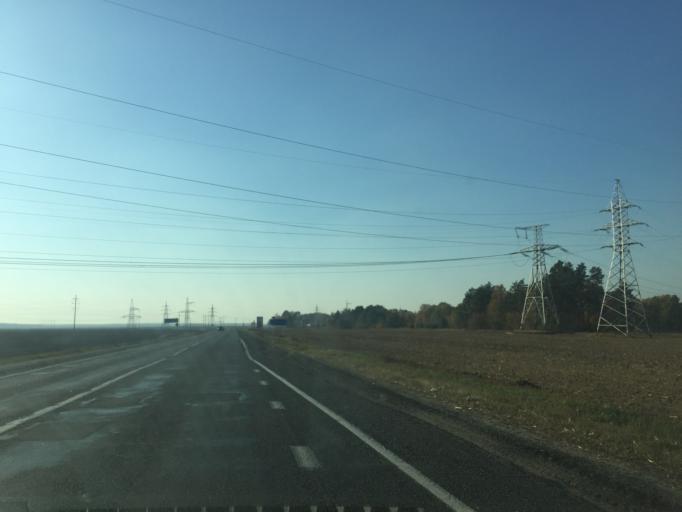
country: BY
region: Gomel
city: Dobrush
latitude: 52.3855
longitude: 31.2904
